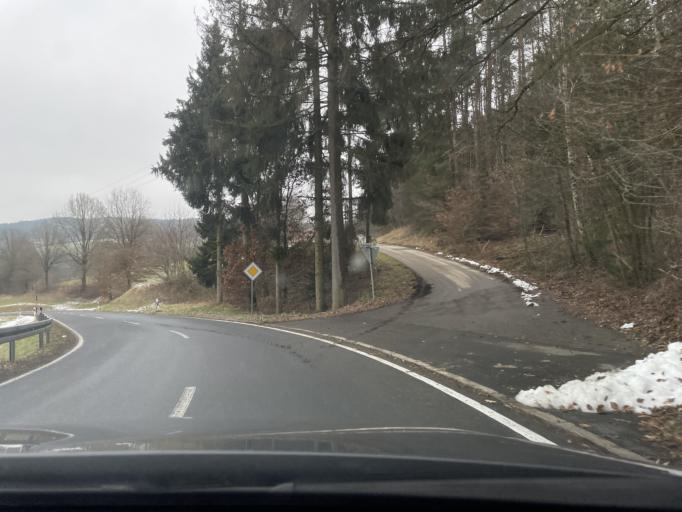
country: DE
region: Bavaria
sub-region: Upper Palatinate
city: Chamerau
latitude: 49.1854
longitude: 12.7208
